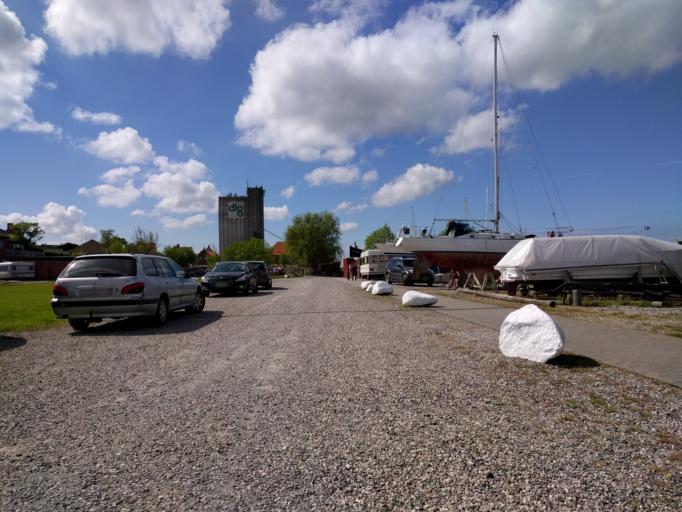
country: DK
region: Zealand
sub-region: Guldborgsund Kommune
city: Stubbekobing
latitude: 54.8907
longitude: 12.0472
